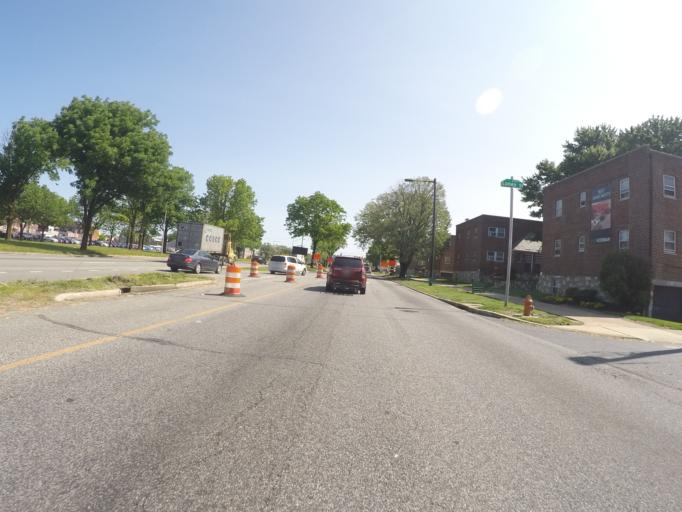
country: US
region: Pennsylvania
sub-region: Montgomery County
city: Rockledge
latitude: 40.0551
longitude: -75.0478
